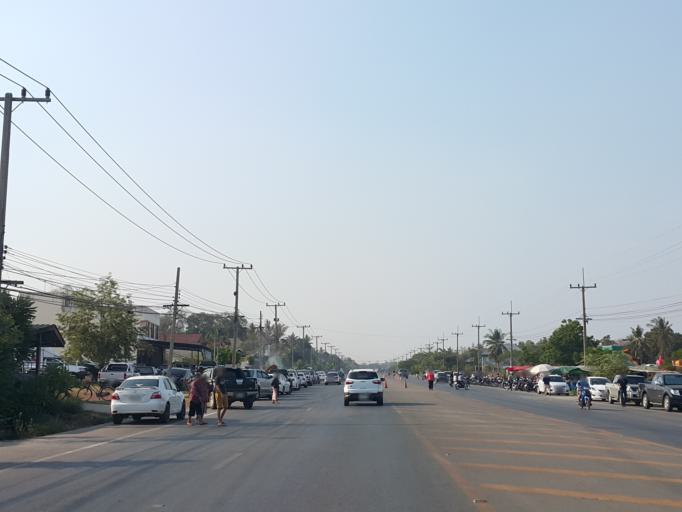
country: TH
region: Phitsanulok
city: Phitsanulok
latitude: 16.9209
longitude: 100.2338
